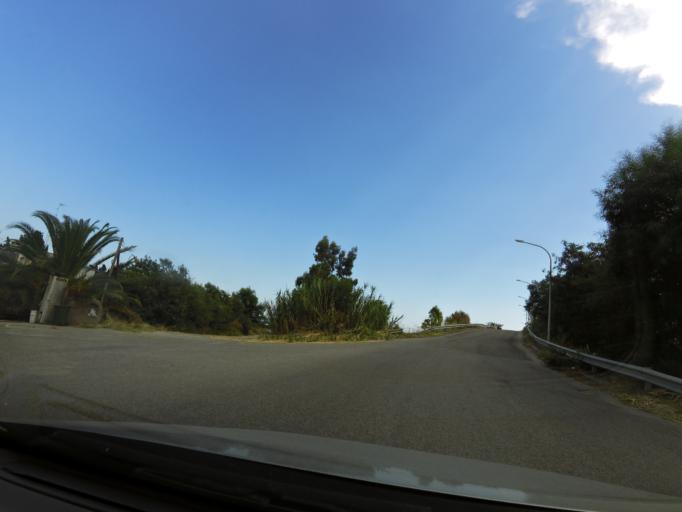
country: IT
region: Calabria
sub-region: Provincia di Reggio Calabria
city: Monasterace Marina
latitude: 38.4198
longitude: 16.5606
